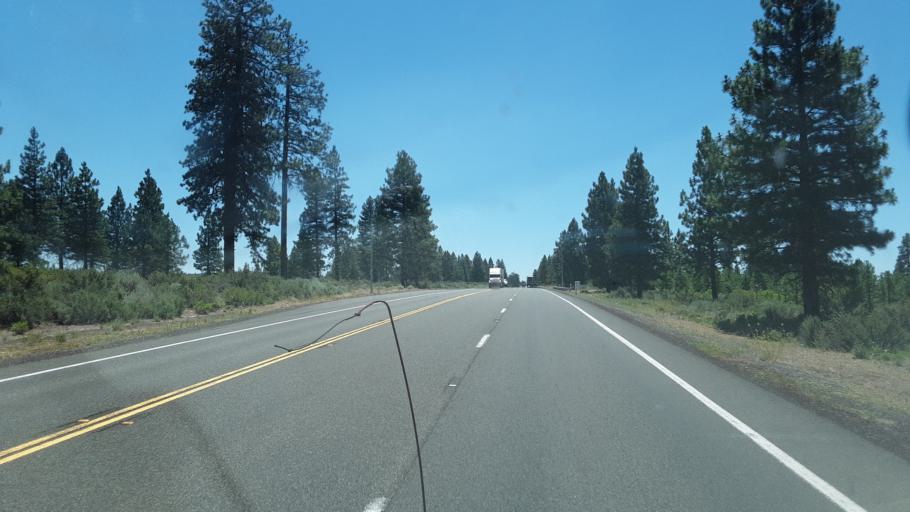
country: US
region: California
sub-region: Siskiyou County
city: Tulelake
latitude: 41.6059
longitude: -121.2085
